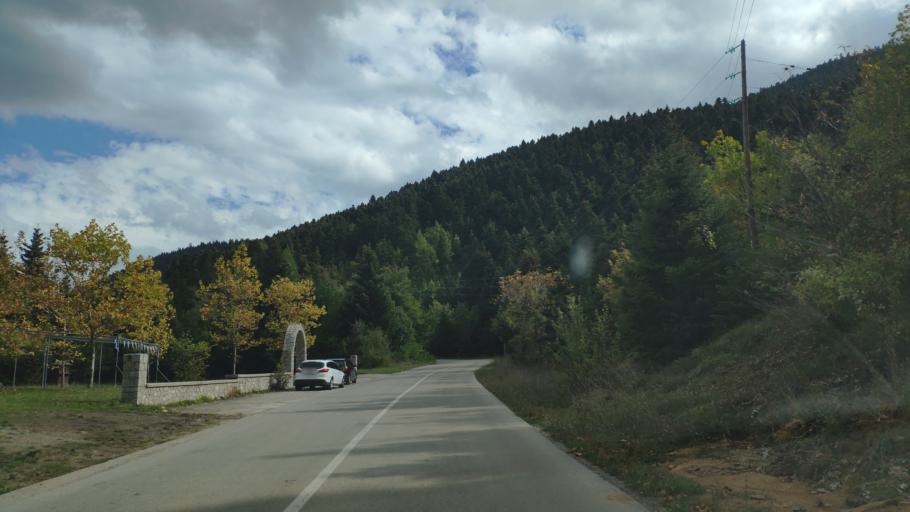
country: GR
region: Central Greece
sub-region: Nomos Fthiotidos
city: Stavros
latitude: 38.7310
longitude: 22.3444
